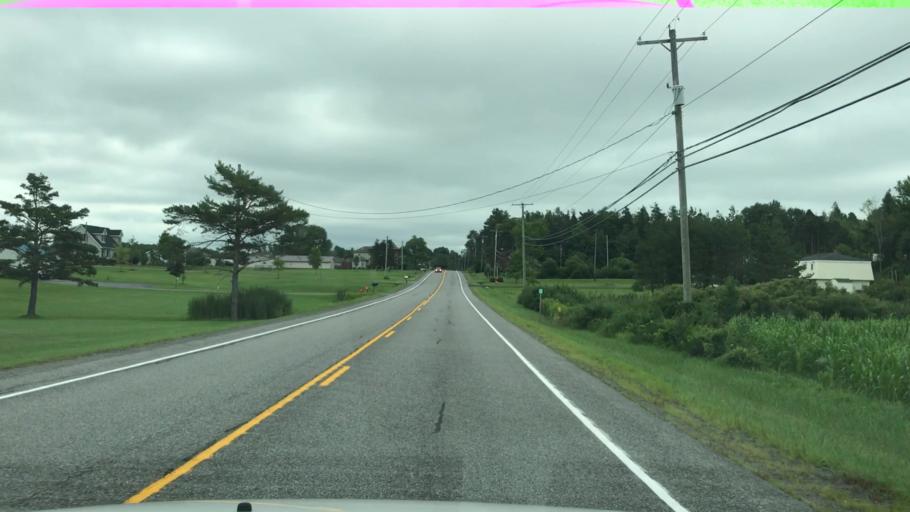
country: US
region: New York
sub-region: Wyoming County
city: Attica
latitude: 42.8362
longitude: -78.3462
